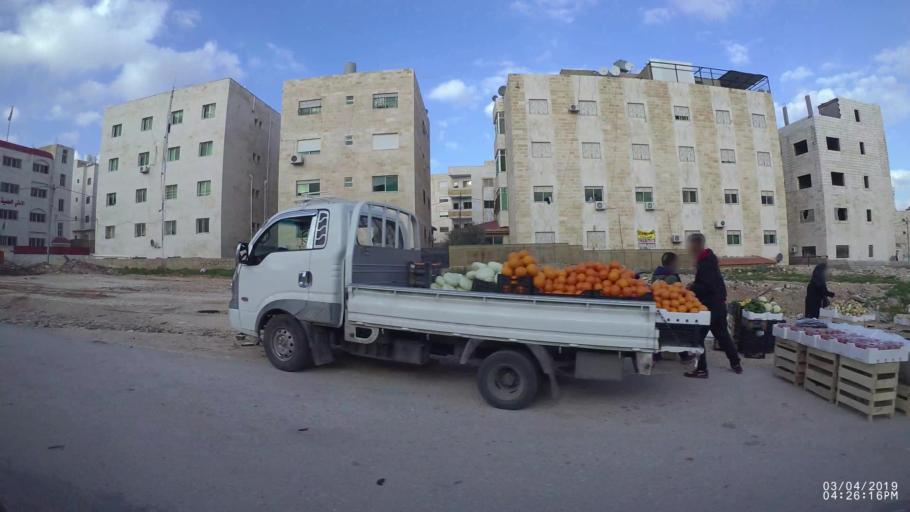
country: JO
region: Amman
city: Al Bunayyat ash Shamaliyah
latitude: 31.9129
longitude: 35.8890
